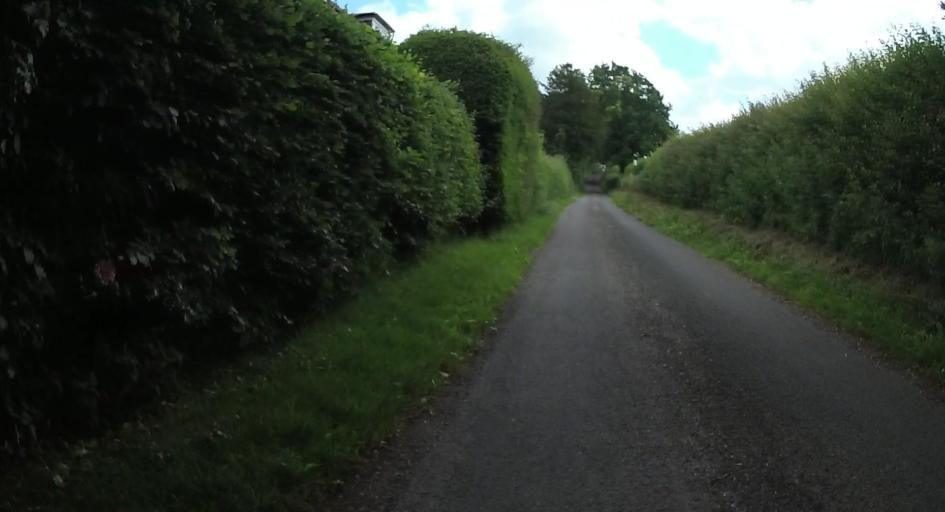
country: GB
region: England
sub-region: Hampshire
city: Four Marks
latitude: 51.1544
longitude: -1.1572
